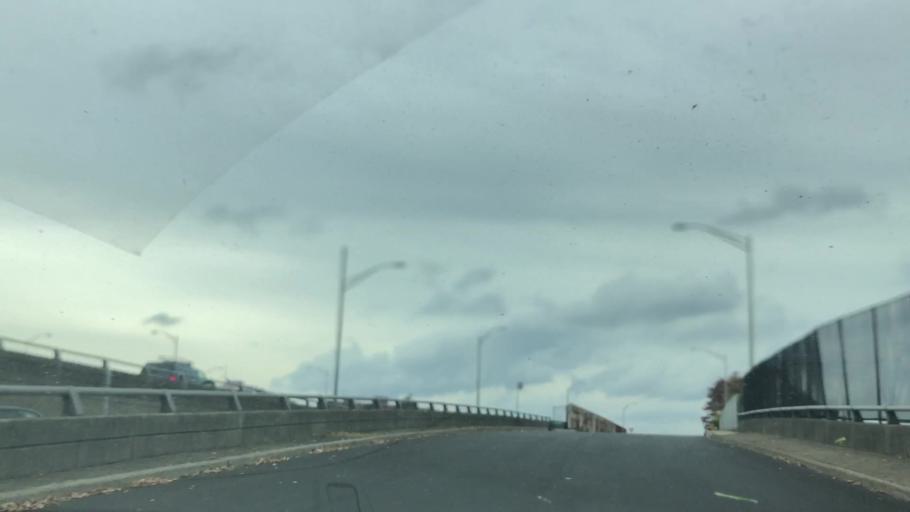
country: US
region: New Jersey
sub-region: Essex County
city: East Orange
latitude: 40.7854
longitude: -74.1992
